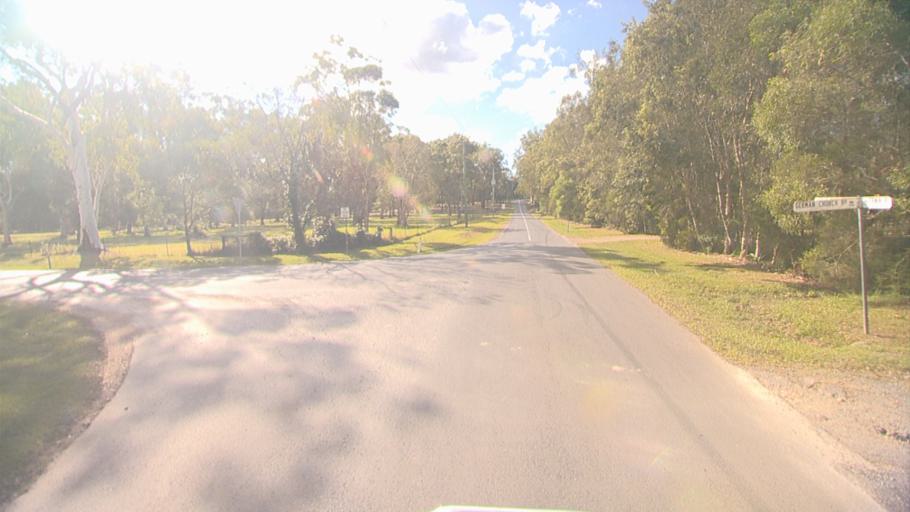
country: AU
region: Queensland
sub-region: Gold Coast
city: Yatala
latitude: -27.6616
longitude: 153.2413
